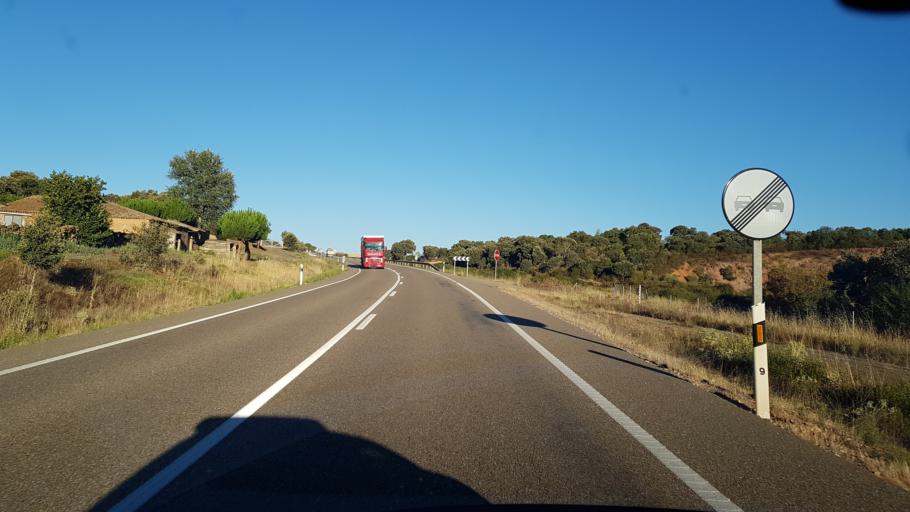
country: ES
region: Castille and Leon
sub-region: Provincia de Zamora
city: Almaraz de Duero
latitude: 41.5352
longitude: -5.9405
